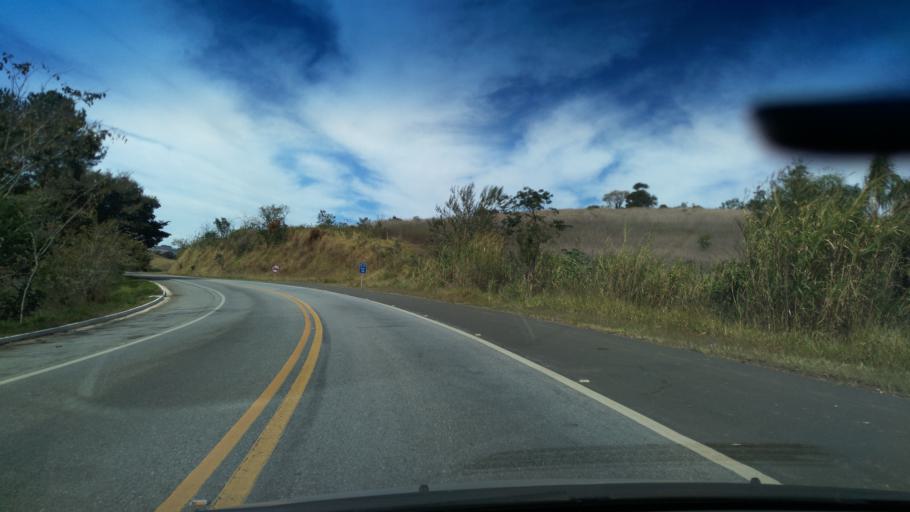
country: BR
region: Minas Gerais
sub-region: Borda Da Mata
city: Borda da Mata
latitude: -22.1448
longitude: -46.1314
